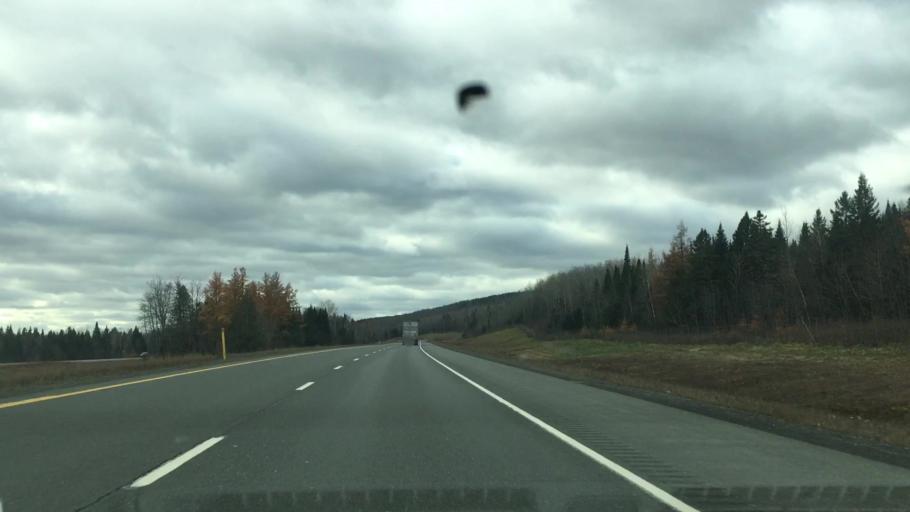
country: US
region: Maine
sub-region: Aroostook County
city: Fort Fairfield
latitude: 46.6573
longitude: -67.7368
